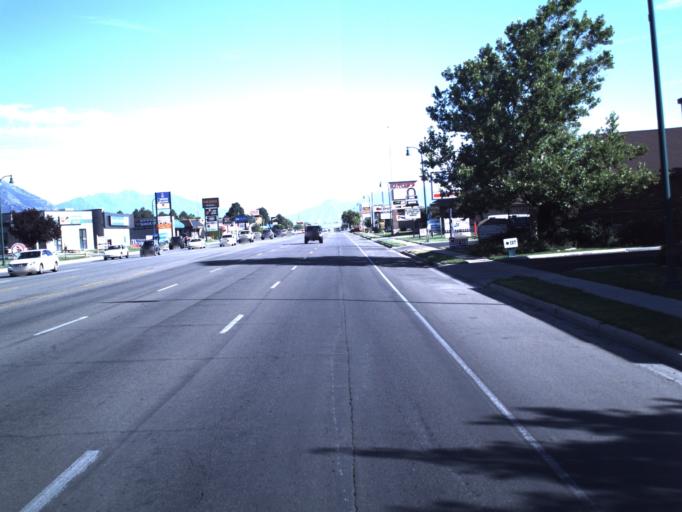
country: US
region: Utah
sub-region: Utah County
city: Orem
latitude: 40.3032
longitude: -111.6978
